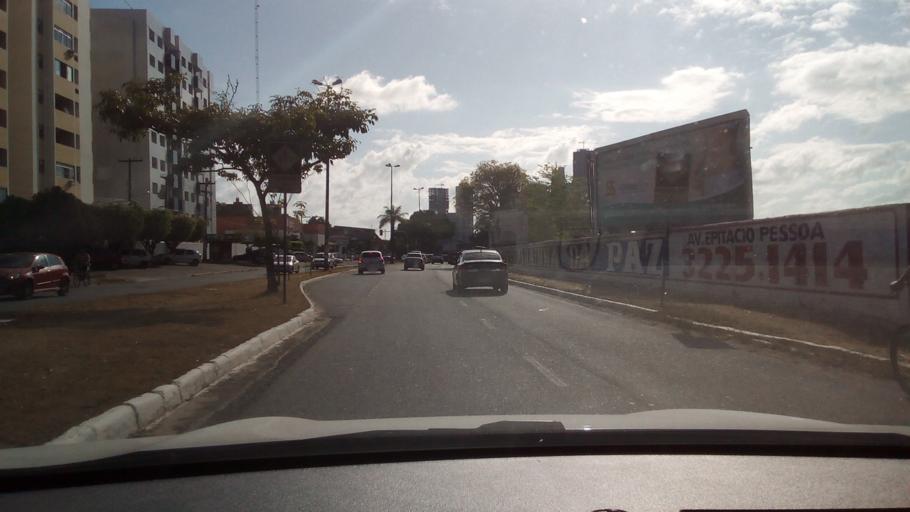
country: BR
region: Paraiba
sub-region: Joao Pessoa
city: Joao Pessoa
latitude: -7.1253
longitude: -34.8424
